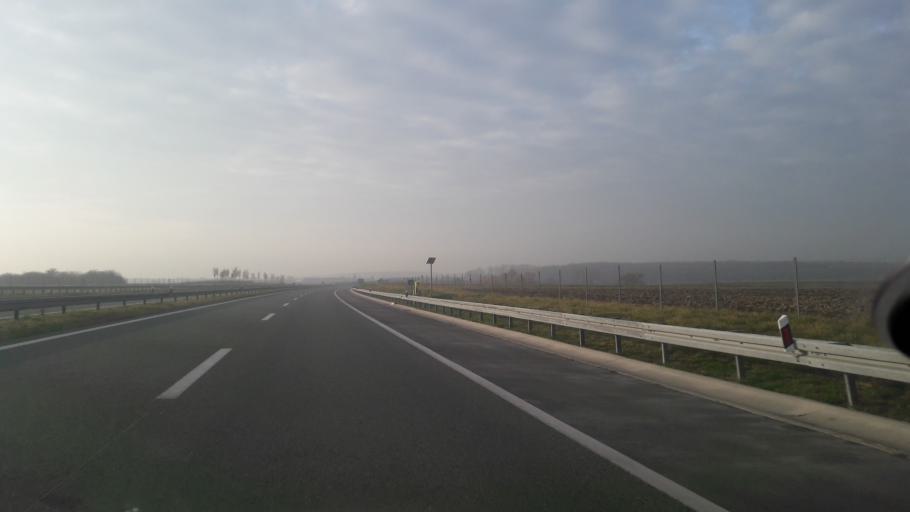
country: HR
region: Osjecko-Baranjska
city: Gorjani
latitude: 45.3436
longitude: 18.3997
